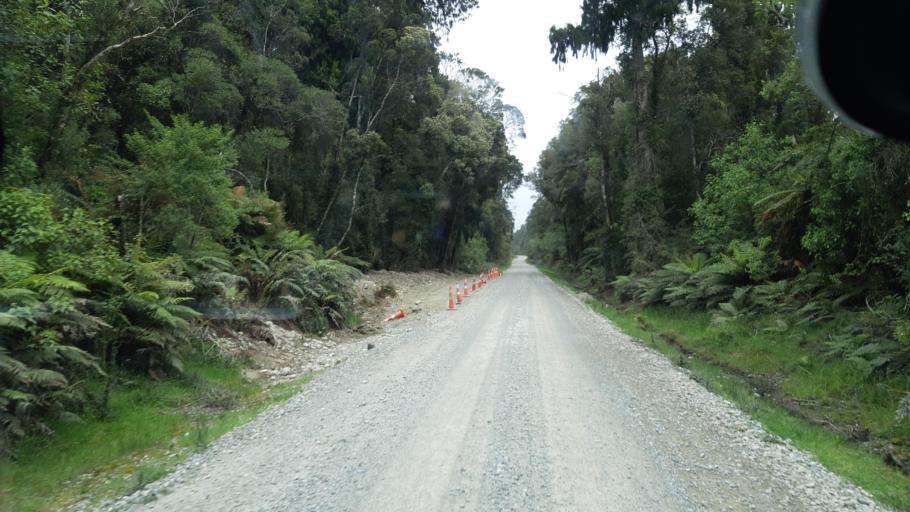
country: NZ
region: West Coast
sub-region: Grey District
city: Greymouth
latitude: -42.6470
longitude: 171.3350
